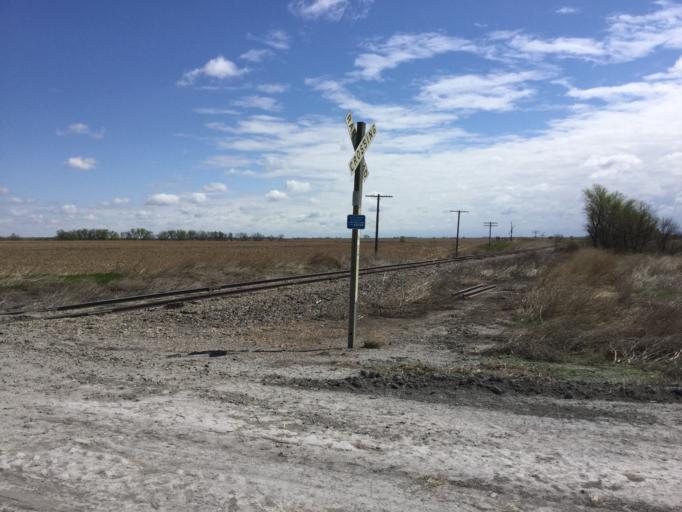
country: US
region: Kansas
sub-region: Phillips County
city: Phillipsburg
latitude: 39.7631
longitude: -99.2072
